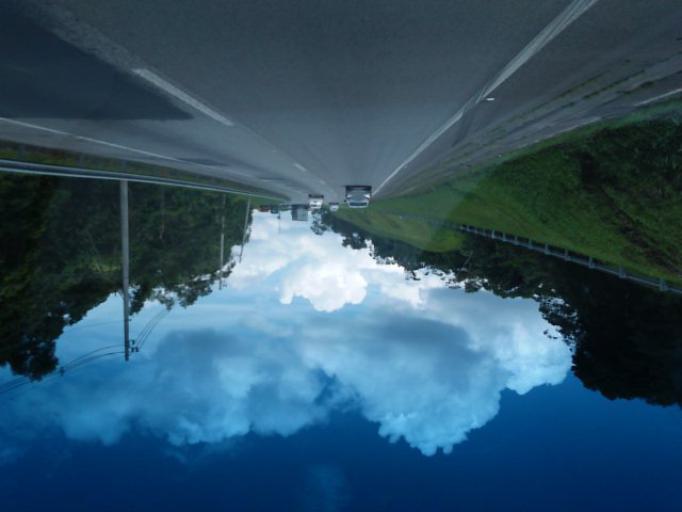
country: BR
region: Sao Paulo
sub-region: Juquitiba
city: Juquitiba
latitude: -23.9587
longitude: -47.1160
